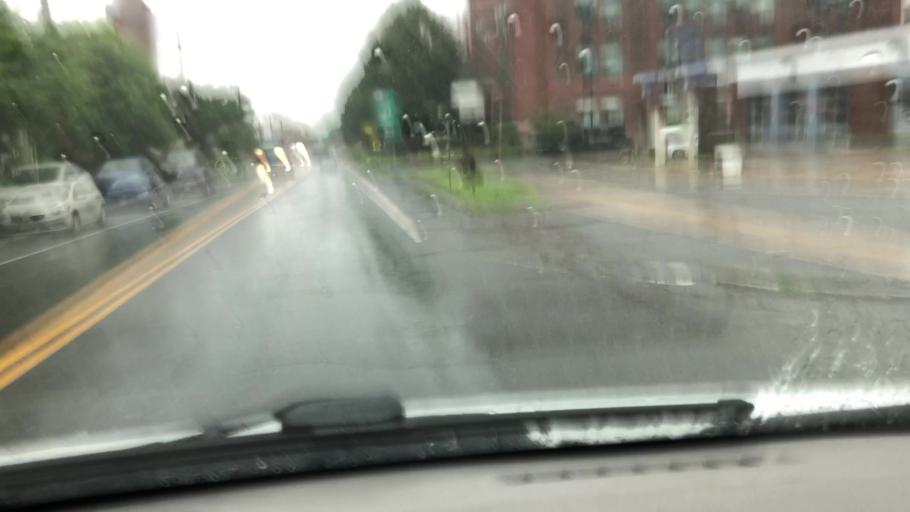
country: US
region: Massachusetts
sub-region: Berkshire County
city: Adams
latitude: 42.6179
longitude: -73.1216
